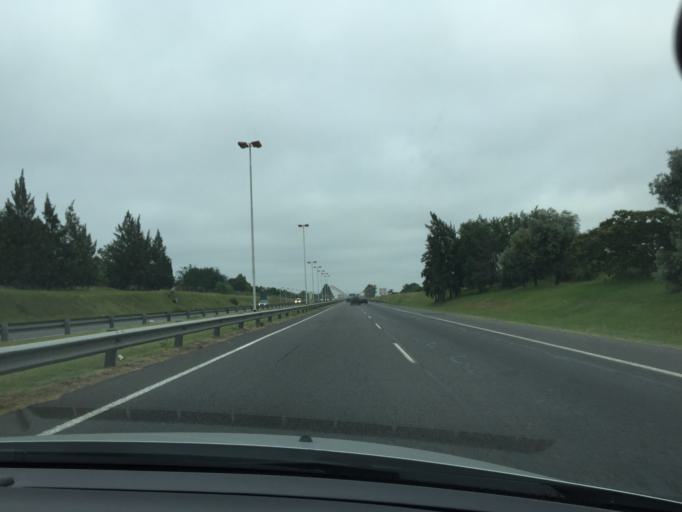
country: AR
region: Buenos Aires
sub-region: Partido de Ezeiza
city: Ezeiza
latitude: -34.8371
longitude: -58.5188
